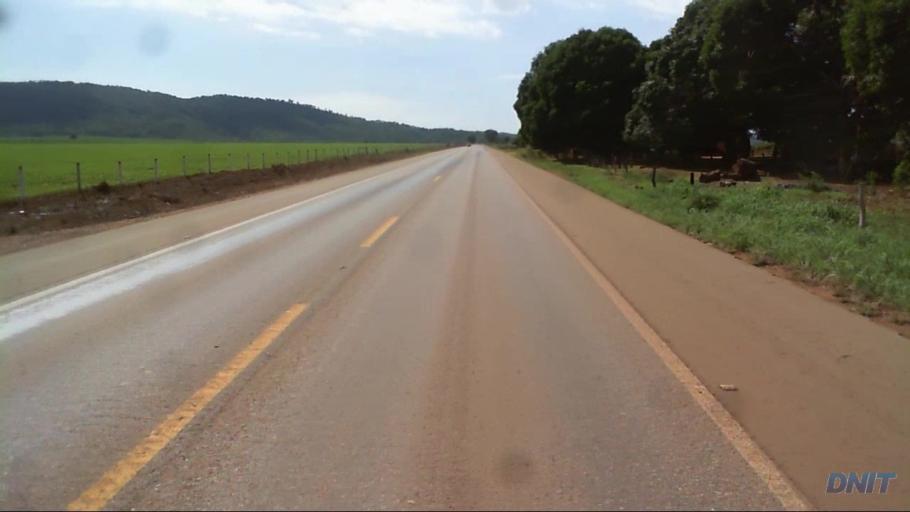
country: BR
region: Goias
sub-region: Barro Alto
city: Barro Alto
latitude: -15.1032
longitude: -48.8490
